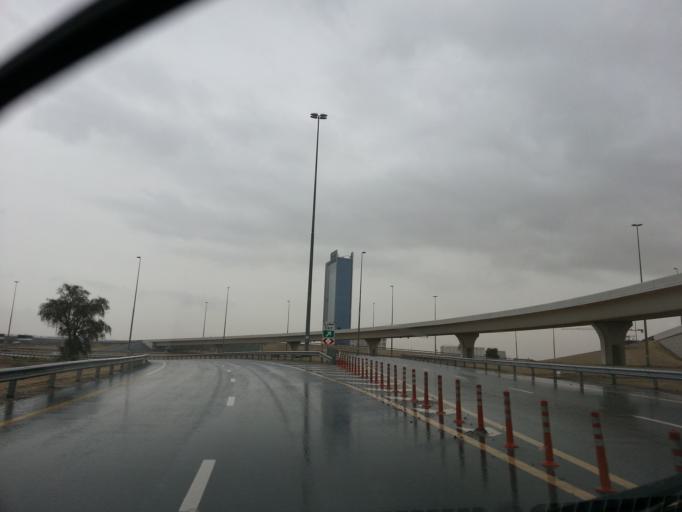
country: AE
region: Dubai
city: Dubai
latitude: 25.0503
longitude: 55.2228
